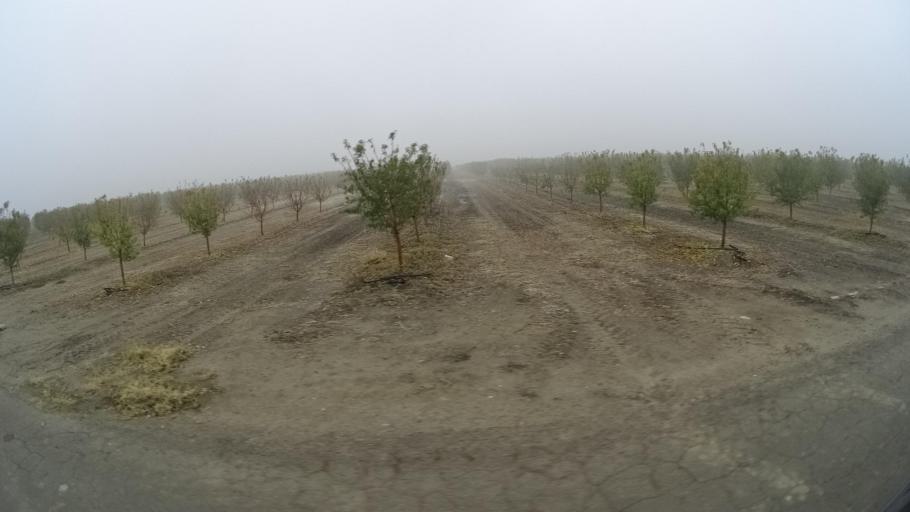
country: US
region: California
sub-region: Kern County
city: Buttonwillow
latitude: 35.4563
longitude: -119.5408
